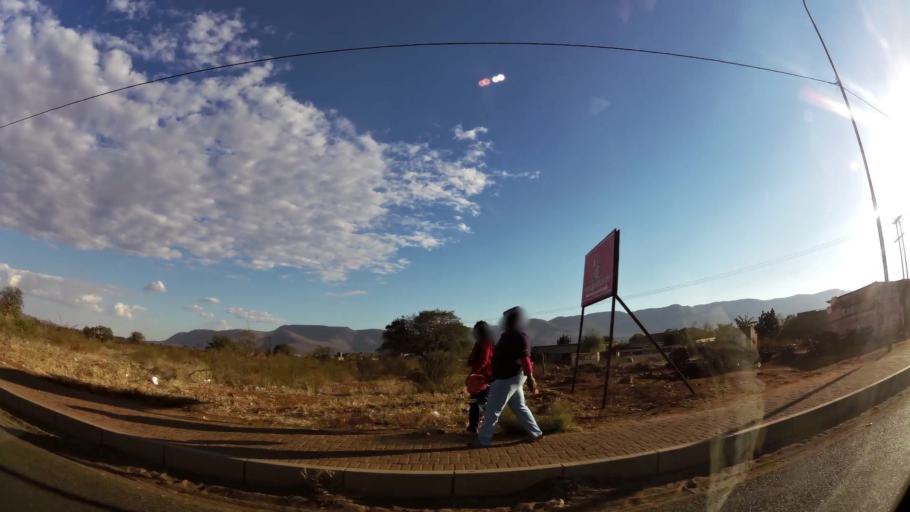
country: ZA
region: Limpopo
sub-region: Waterberg District Municipality
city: Mokopane
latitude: -24.1664
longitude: 28.9947
